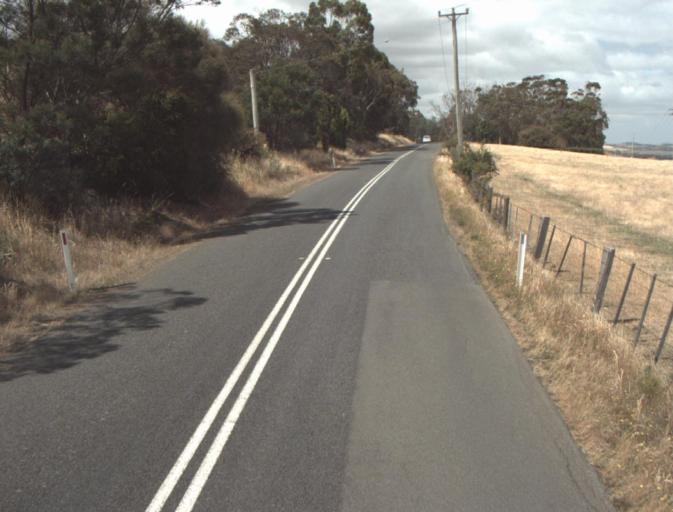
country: AU
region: Tasmania
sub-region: Northern Midlands
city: Evandale
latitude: -41.5123
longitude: 147.2906
